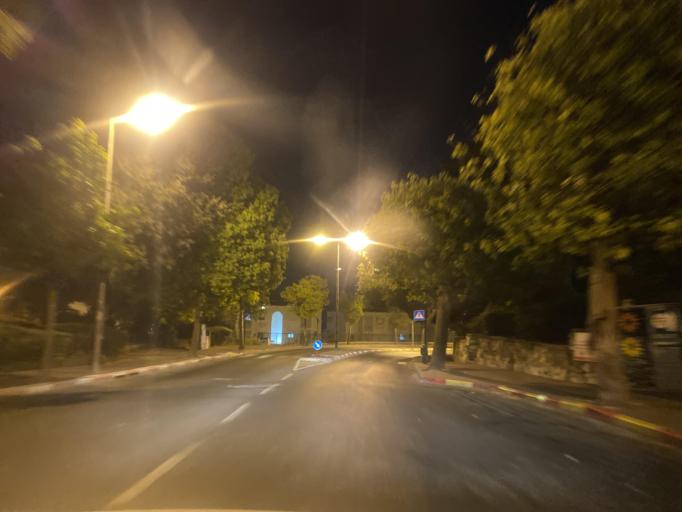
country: IL
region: Haifa
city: Daliyat el Karmil
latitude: 32.6434
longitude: 35.0891
